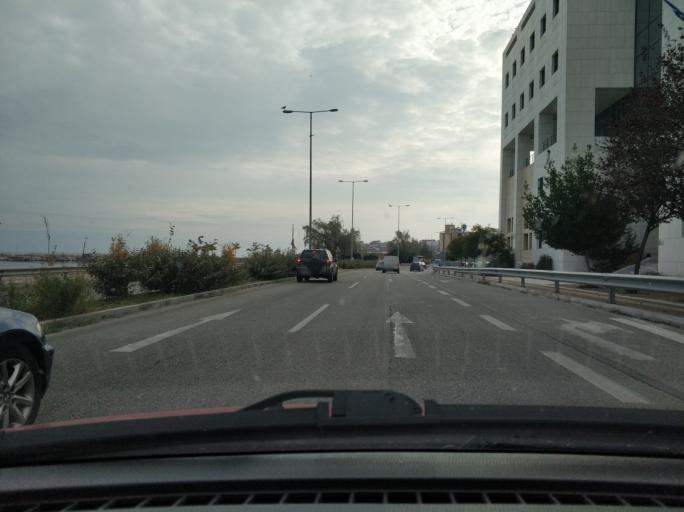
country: GR
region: East Macedonia and Thrace
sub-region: Nomos Kavalas
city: Kavala
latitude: 40.9303
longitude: 24.3916
